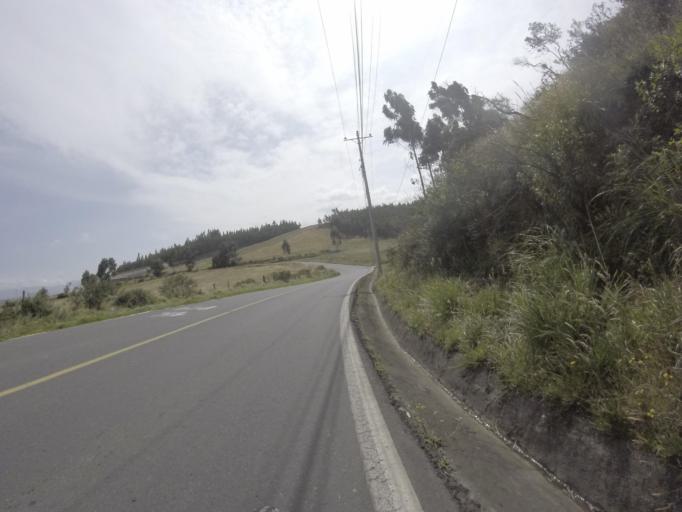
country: EC
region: Pichincha
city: Cayambe
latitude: 0.1228
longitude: -78.0843
